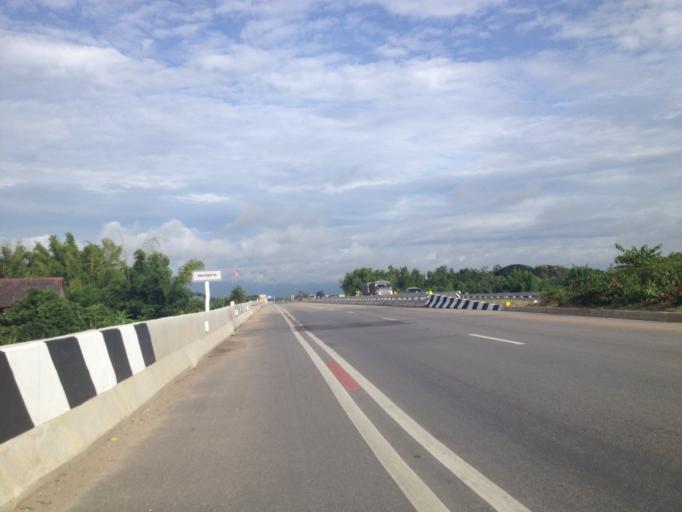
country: TH
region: Lamphun
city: Pa Sang
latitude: 18.5355
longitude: 98.8588
